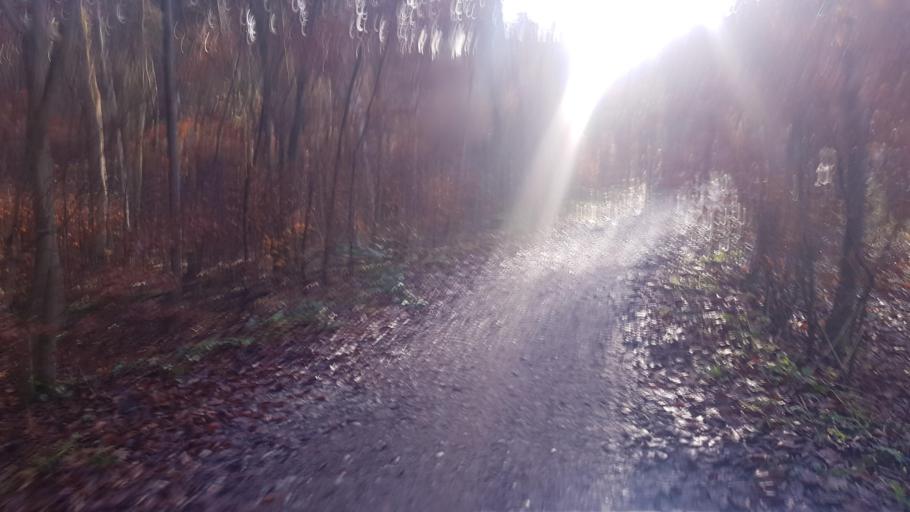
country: DE
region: Bavaria
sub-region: Upper Bavaria
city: Gauting
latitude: 48.0410
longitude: 11.3738
